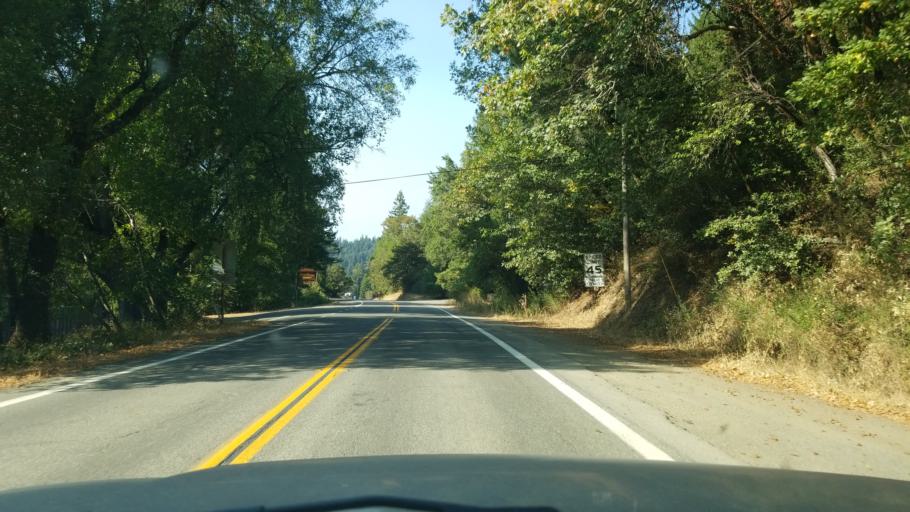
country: US
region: California
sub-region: Humboldt County
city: Redway
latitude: 40.2073
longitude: -123.7855
